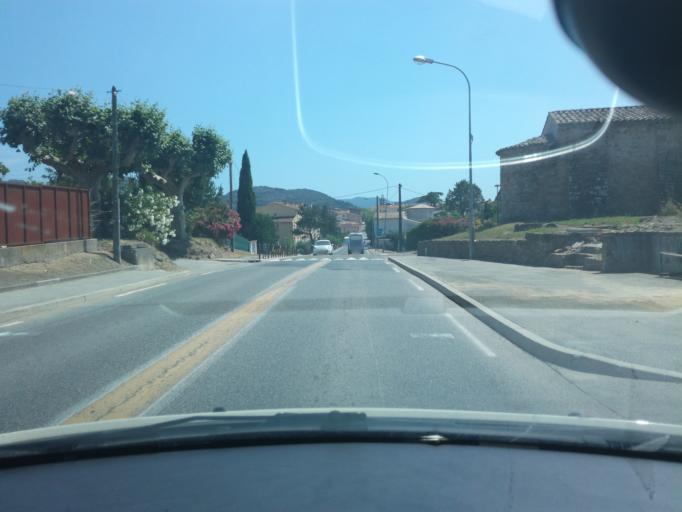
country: FR
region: Provence-Alpes-Cote d'Azur
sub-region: Departement du Var
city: Le Muy
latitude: 43.4777
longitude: 6.5666
